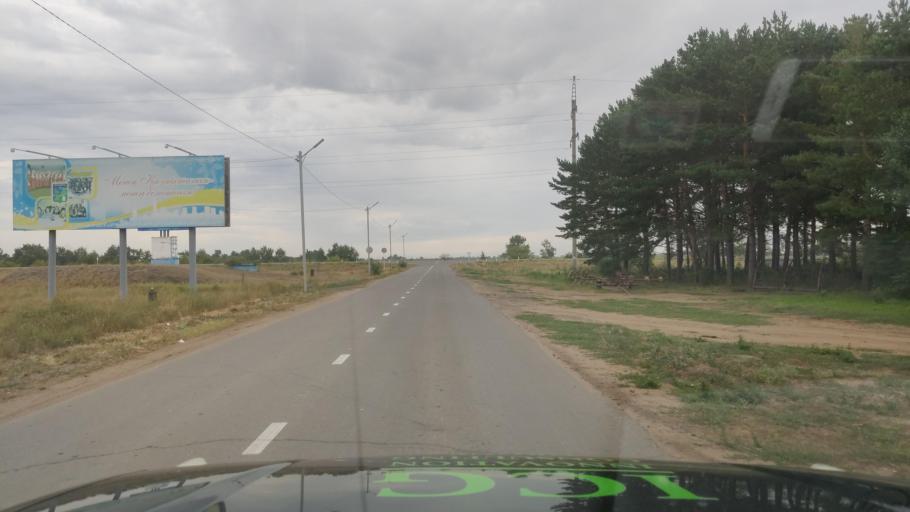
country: KZ
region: Pavlodar
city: Leninskiy
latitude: 52.5402
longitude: 76.8105
